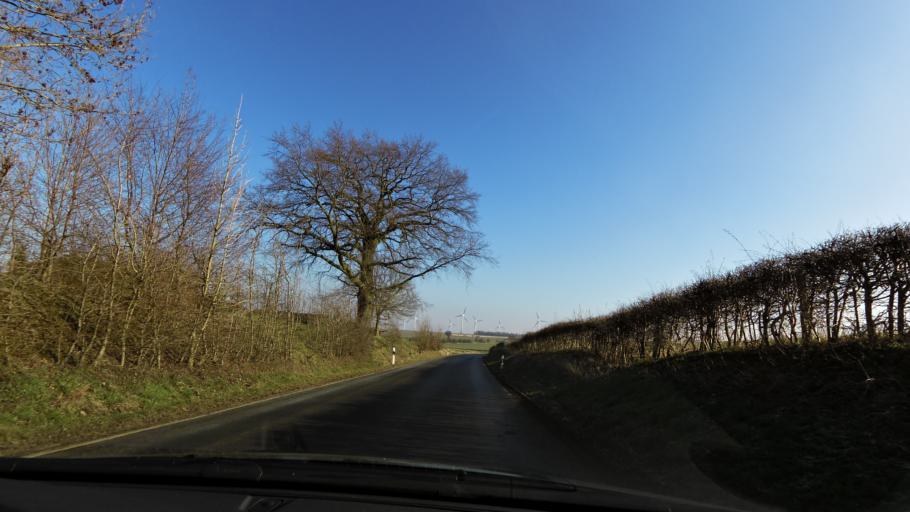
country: NL
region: Limburg
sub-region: Gemeente Vaals
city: Vaals
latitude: 50.7967
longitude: 6.0029
